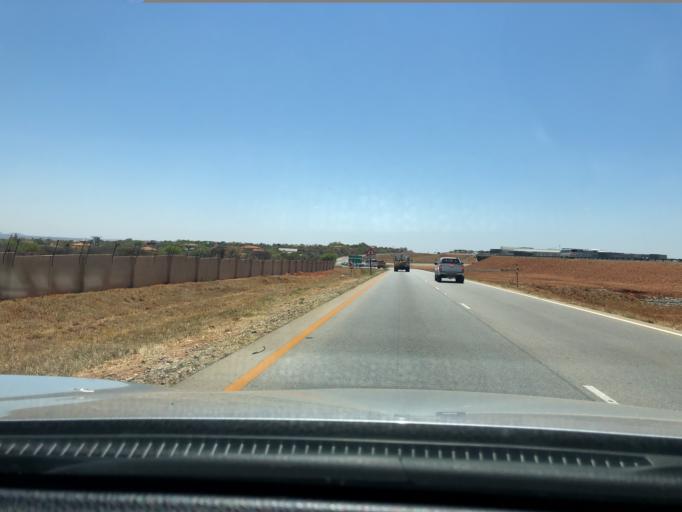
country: ZA
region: Limpopo
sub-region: Capricorn District Municipality
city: Polokwane
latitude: -23.8816
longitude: 29.5073
